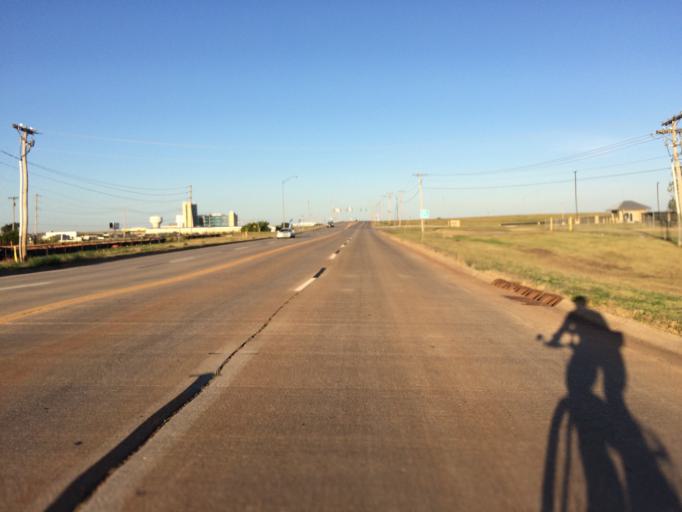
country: US
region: Oklahoma
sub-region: Cleveland County
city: Norman
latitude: 35.2621
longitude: -97.4794
